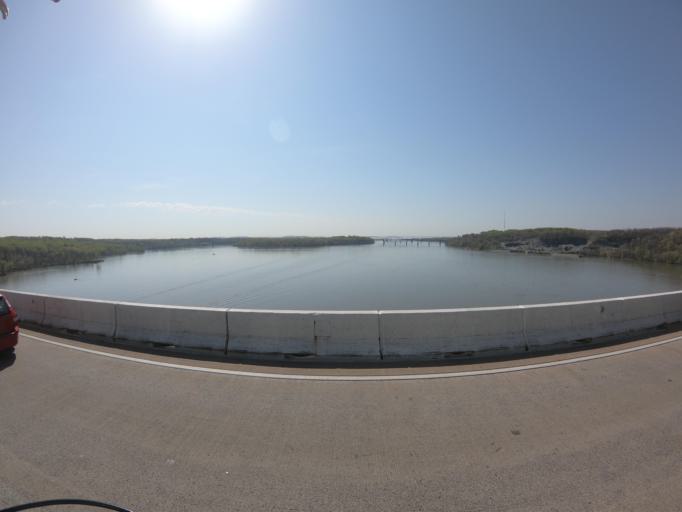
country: US
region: Maryland
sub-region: Harford County
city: Havre de Grace
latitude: 39.5824
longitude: -76.1037
